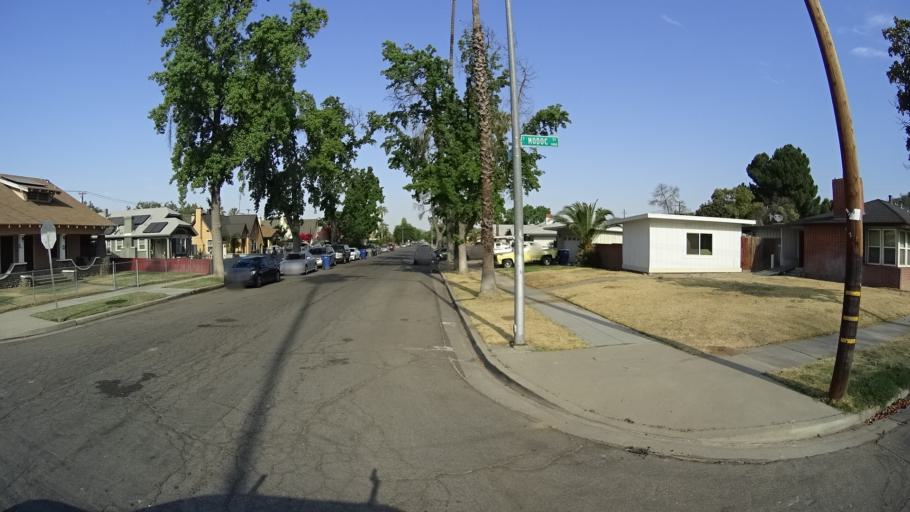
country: US
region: California
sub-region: Fresno County
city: Fresno
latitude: 36.7276
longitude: -119.8102
